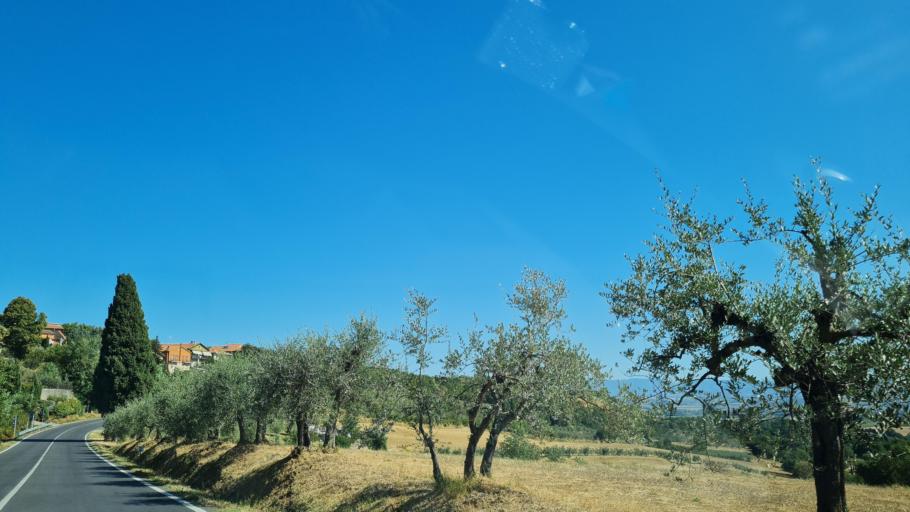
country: IT
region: Tuscany
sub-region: Provincia di Siena
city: Sant'Albino
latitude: 43.0603
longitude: 11.8173
